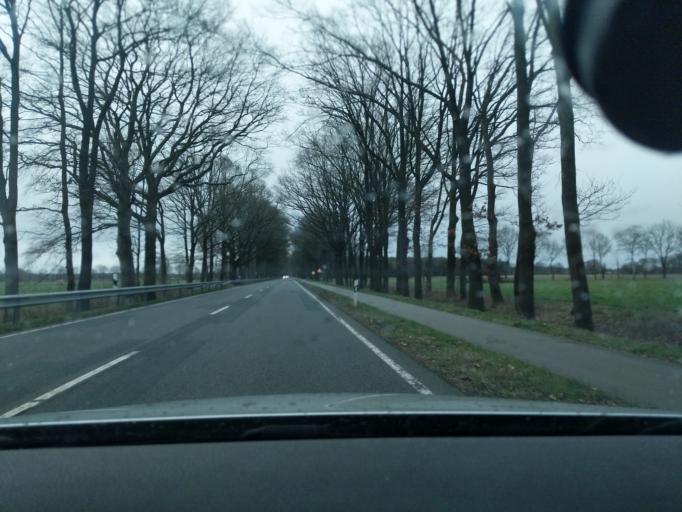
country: DE
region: Lower Saxony
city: Oldendorf
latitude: 53.5333
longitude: 9.2547
